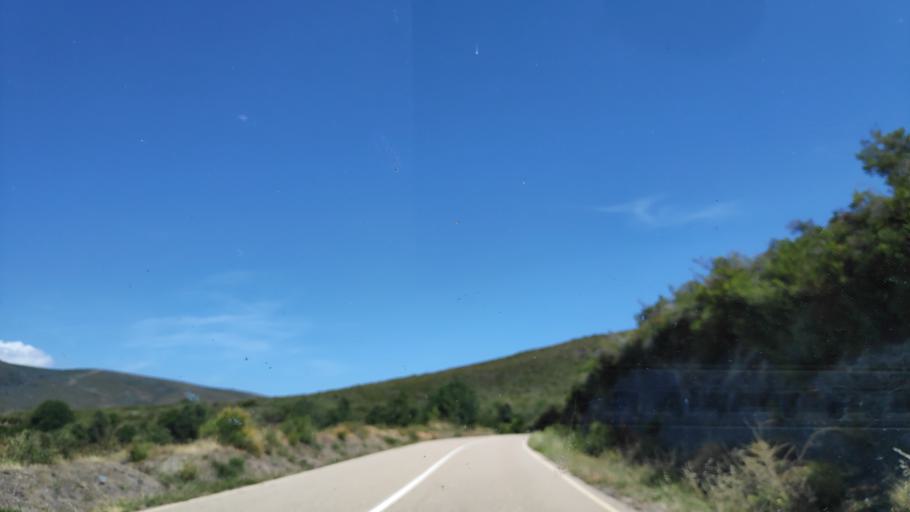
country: ES
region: Castille and Leon
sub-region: Provincia de Zamora
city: Requejo
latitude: 41.9755
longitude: -6.7131
